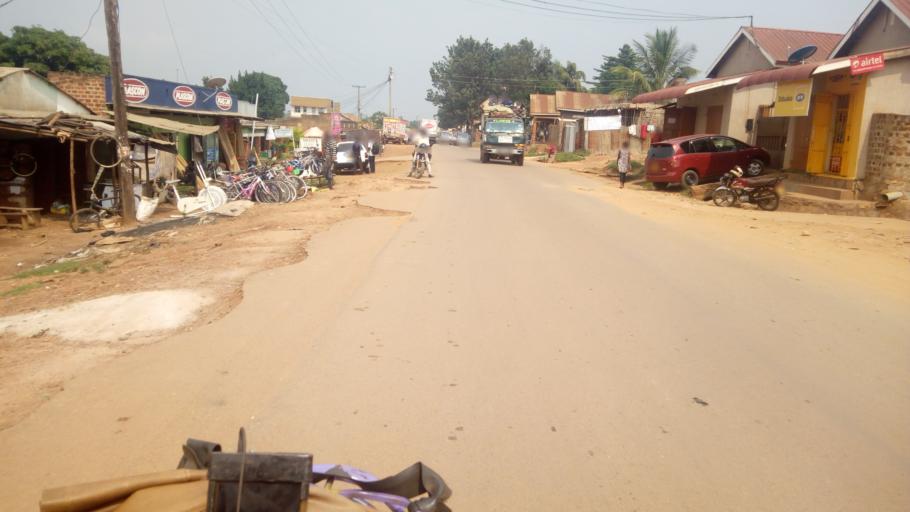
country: UG
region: Central Region
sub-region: Wakiso District
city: Kireka
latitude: 0.3175
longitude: 32.6496
